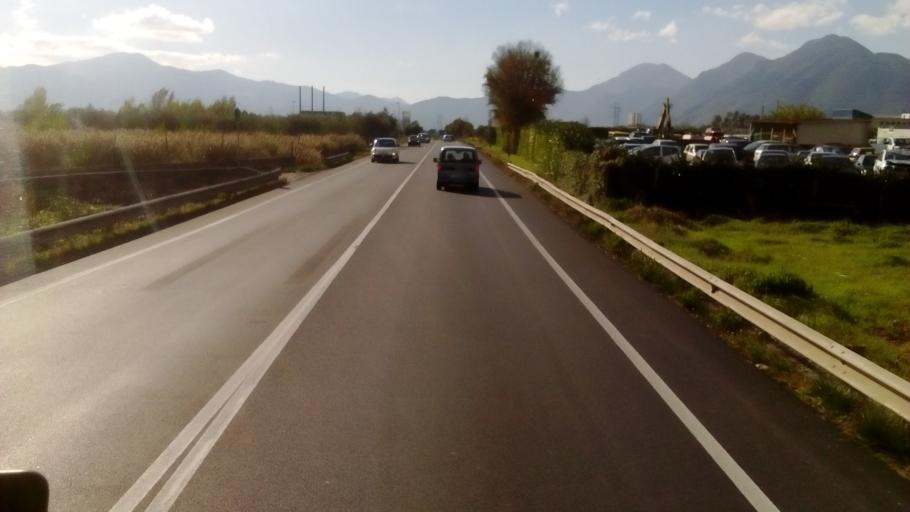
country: IT
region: Molise
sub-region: Provincia di Isernia
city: Taverna Ravindola
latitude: 41.5146
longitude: 14.1207
